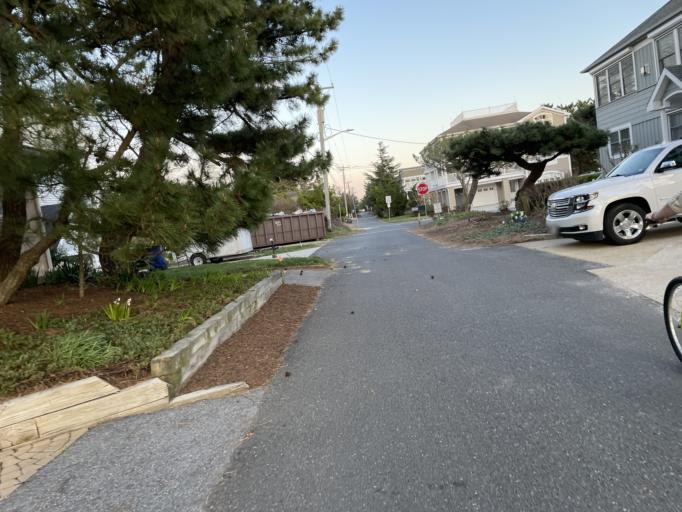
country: US
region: Delaware
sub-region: Sussex County
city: Lewes
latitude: 38.7882
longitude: -75.1560
